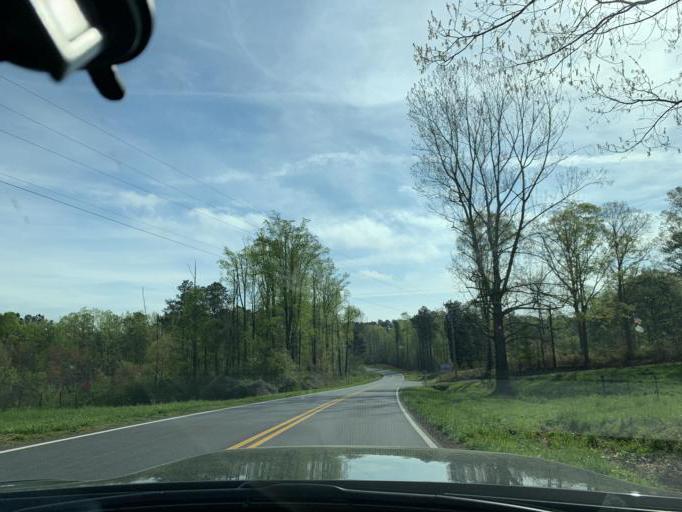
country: US
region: Georgia
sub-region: Forsyth County
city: Cumming
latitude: 34.2585
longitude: -84.1317
